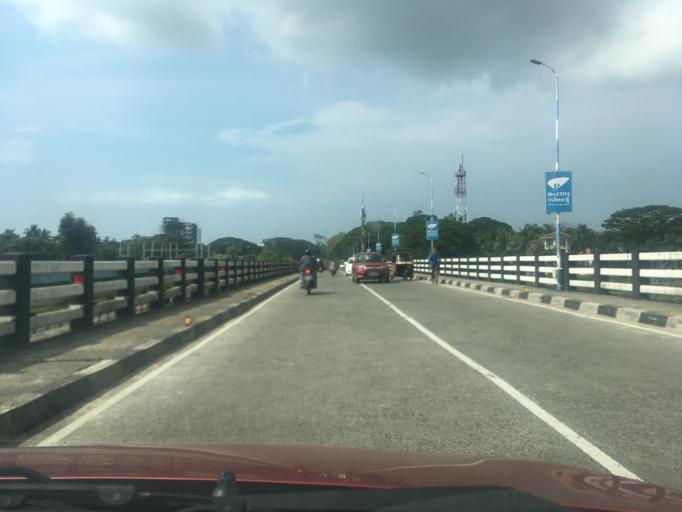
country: IN
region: Kerala
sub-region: Ernakulam
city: Cochin
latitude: 9.9457
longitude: 76.2863
